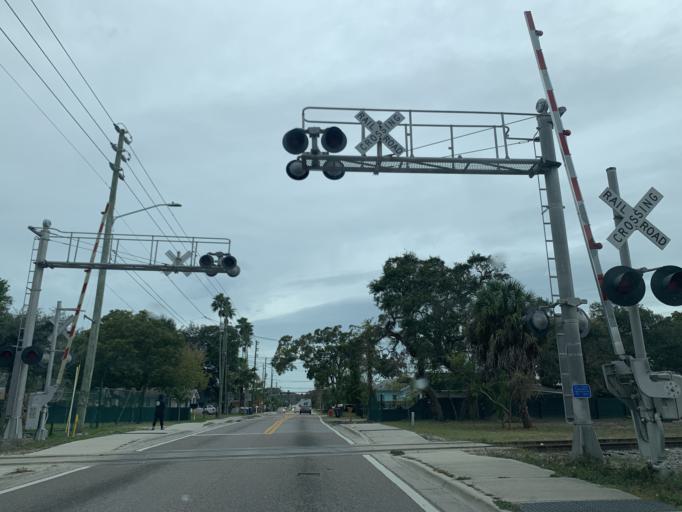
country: US
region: Florida
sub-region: Pinellas County
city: Belleair
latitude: 27.9352
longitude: -82.7938
